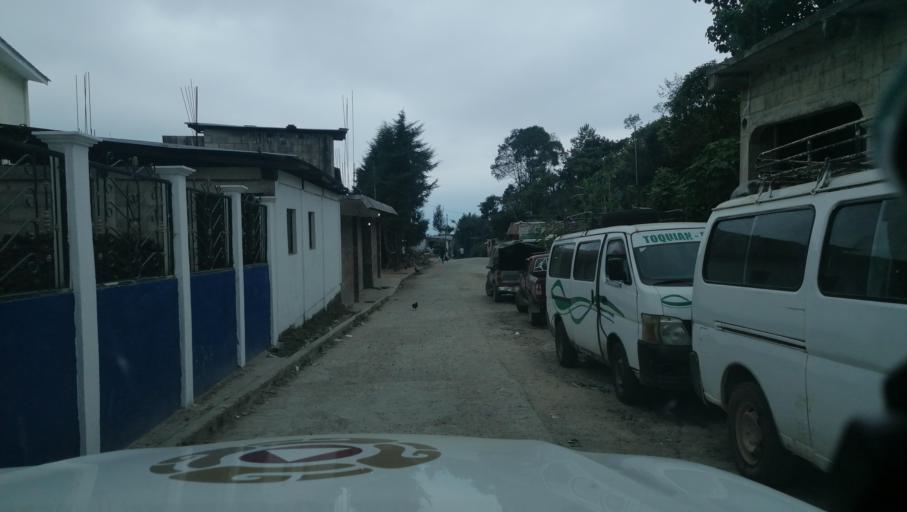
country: GT
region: San Marcos
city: Tacana
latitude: 15.2018
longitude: -92.1776
